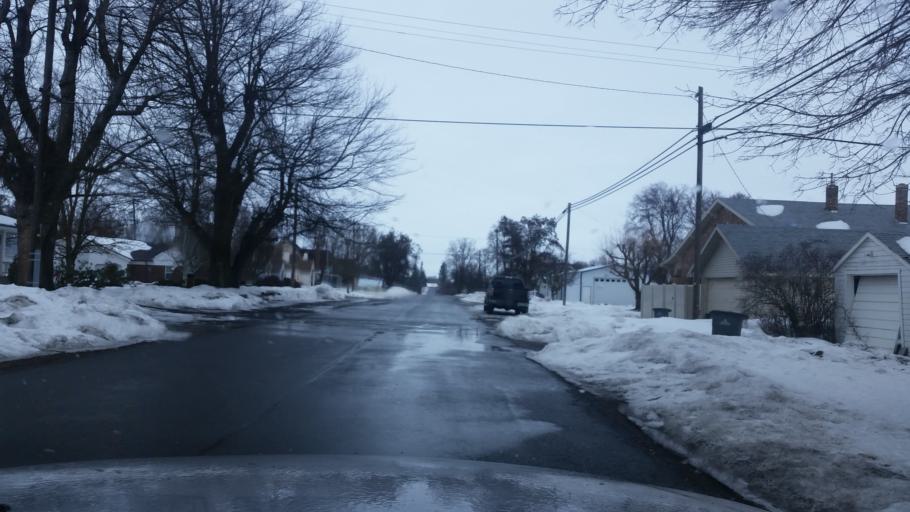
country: US
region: Washington
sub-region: Lincoln County
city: Davenport
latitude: 47.6502
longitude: -118.1523
